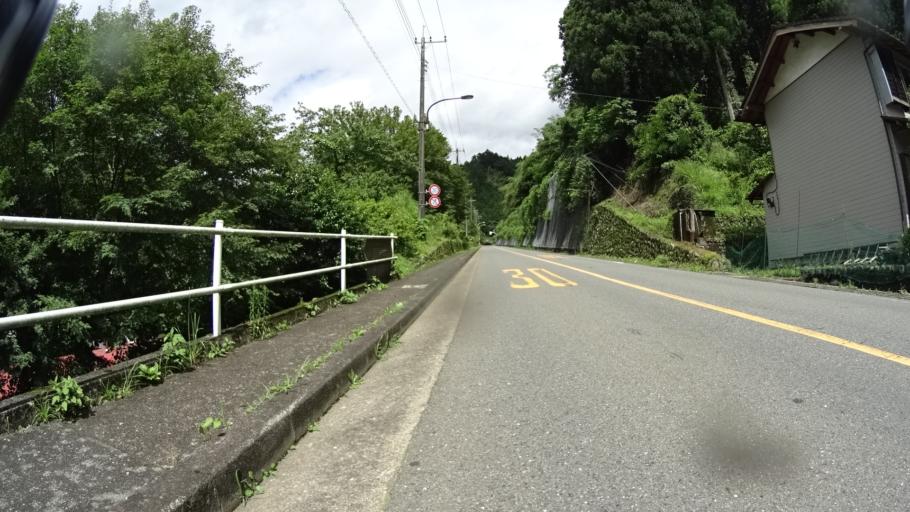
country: JP
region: Tokyo
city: Ome
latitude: 35.8376
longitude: 139.2017
